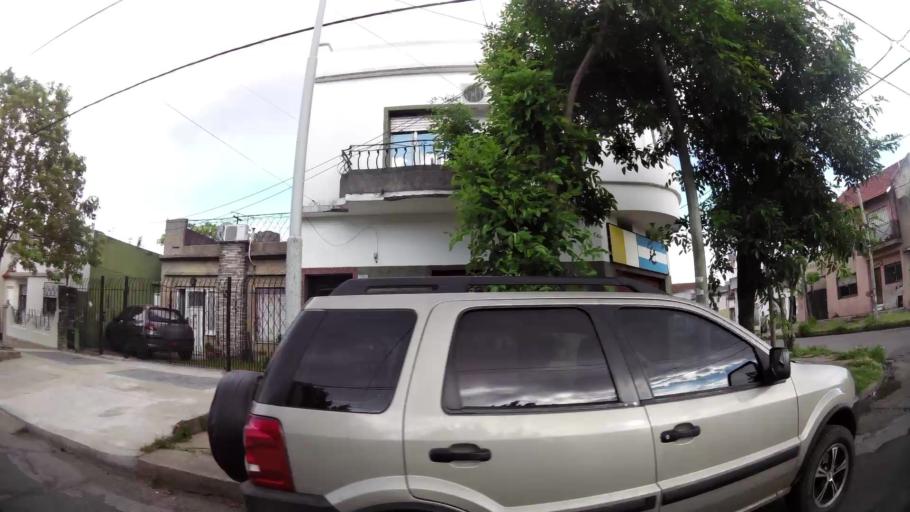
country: AR
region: Buenos Aires
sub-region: Partido de Lanus
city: Lanus
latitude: -34.6922
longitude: -58.3679
